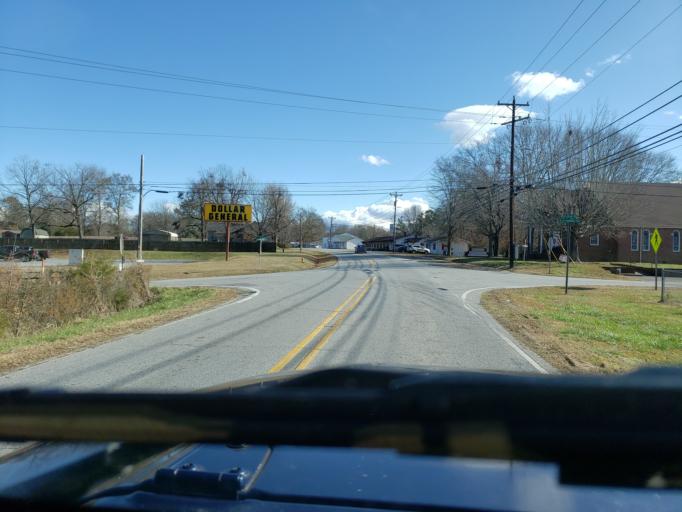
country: US
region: North Carolina
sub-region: Cleveland County
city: White Plains
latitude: 35.1780
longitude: -81.4563
